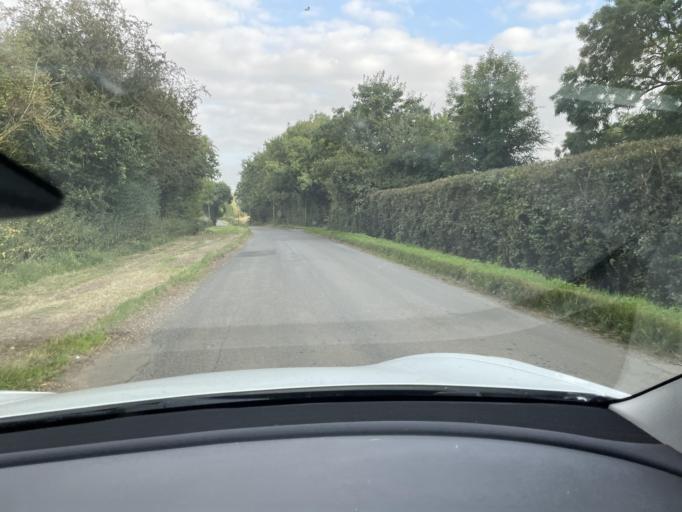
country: GB
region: England
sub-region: Northamptonshire
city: Brixworth
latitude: 52.3928
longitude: -0.9668
